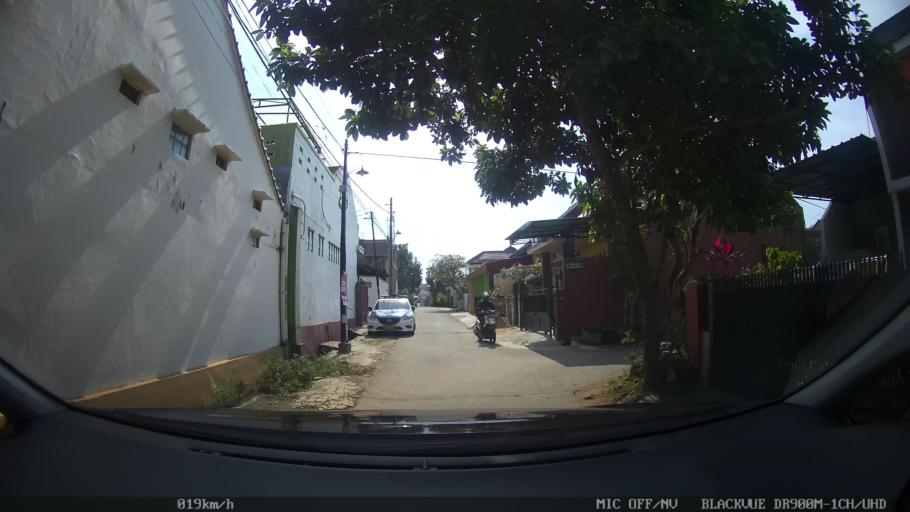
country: ID
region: Lampung
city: Kedaton
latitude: -5.3848
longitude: 105.2382
